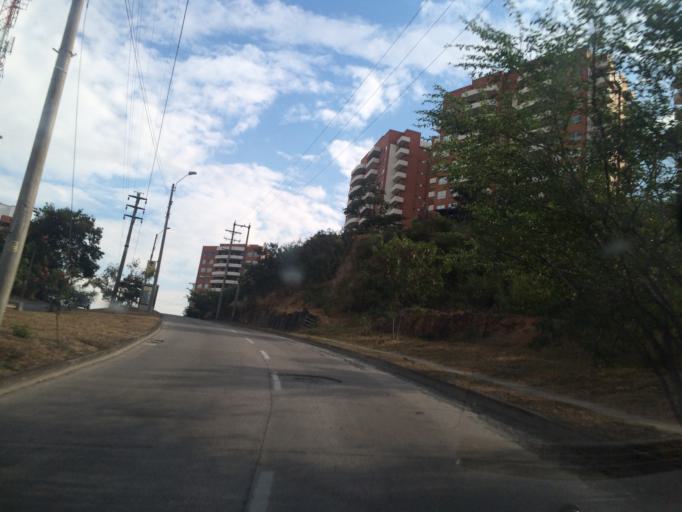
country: CO
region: Valle del Cauca
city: Cali
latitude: 3.4334
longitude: -76.5507
